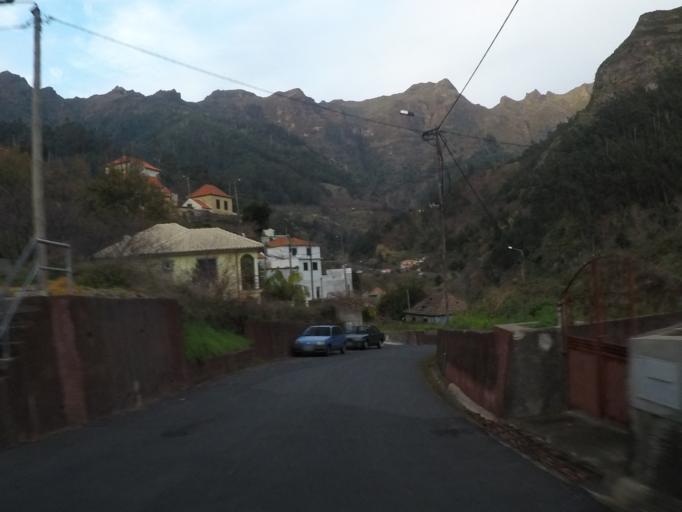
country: PT
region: Madeira
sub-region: Camara de Lobos
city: Curral das Freiras
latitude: 32.7329
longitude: -16.9709
